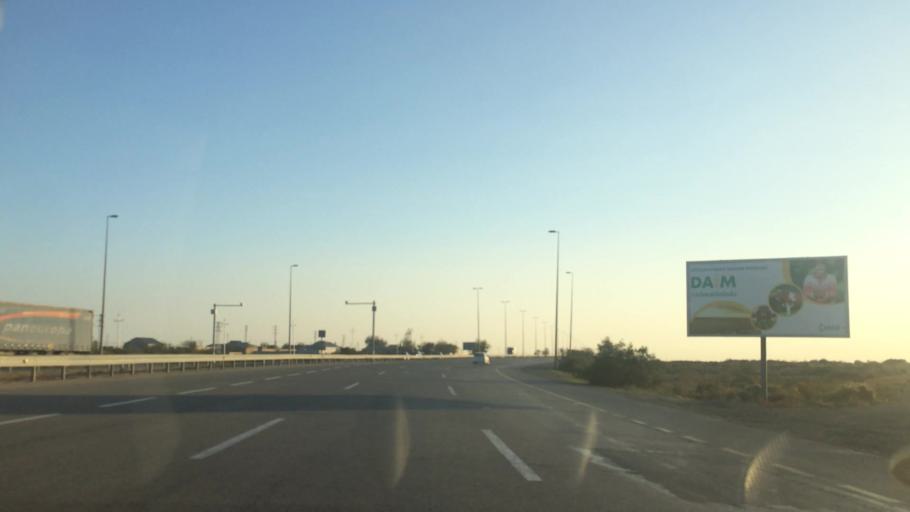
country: AZ
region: Baki
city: Qobustan
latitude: 39.9913
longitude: 49.4302
